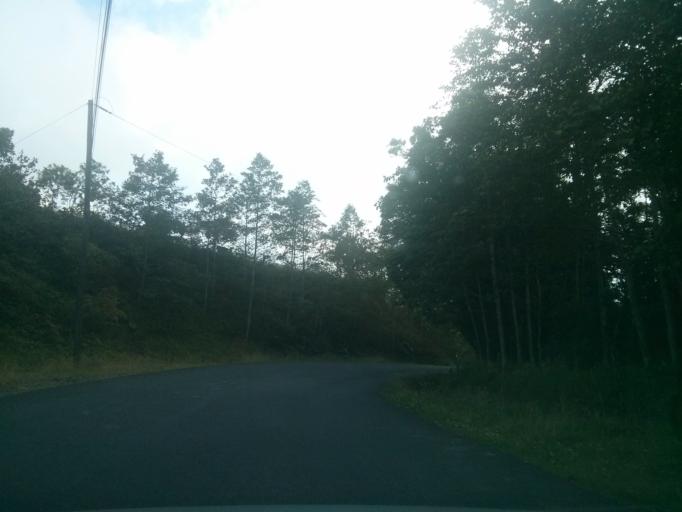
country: CR
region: Heredia
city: Santo Domingo
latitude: 10.1445
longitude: -84.1580
